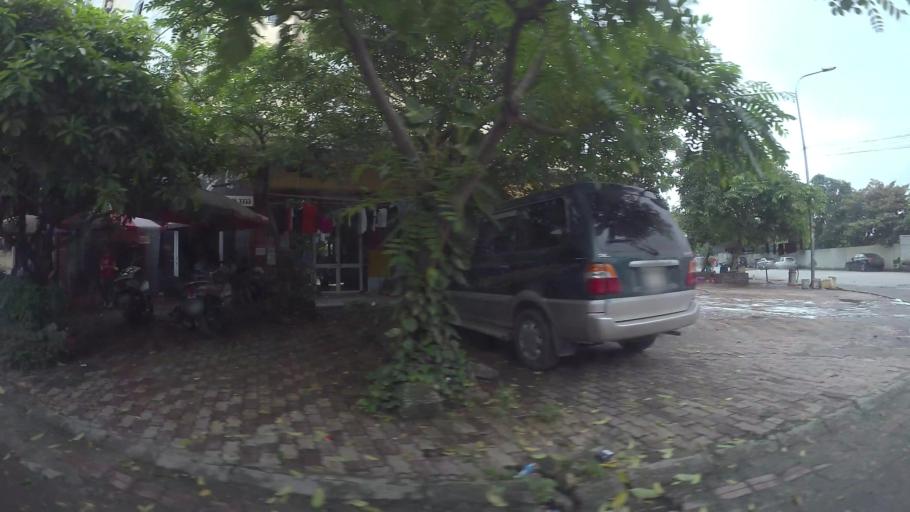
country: VN
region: Ha Noi
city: Van Dien
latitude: 20.9706
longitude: 105.8460
